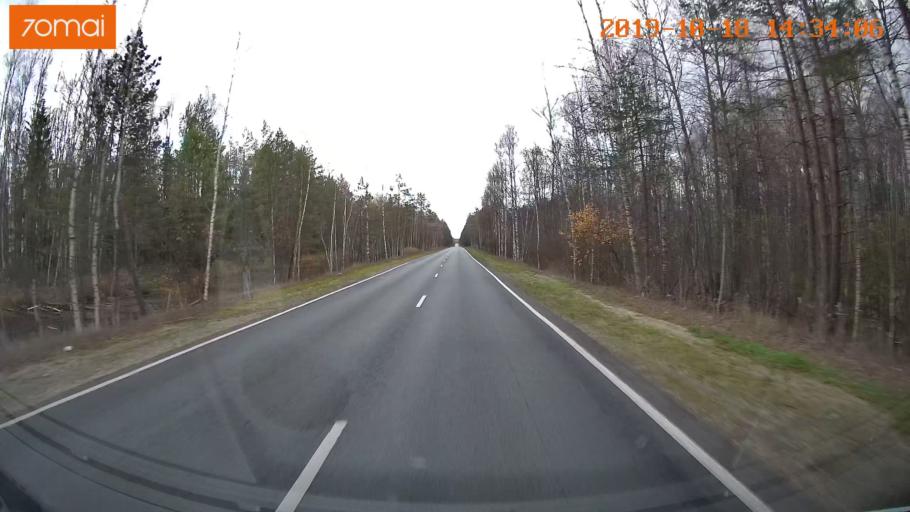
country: RU
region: Vladimir
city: Velikodvorskiy
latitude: 55.2087
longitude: 40.6097
